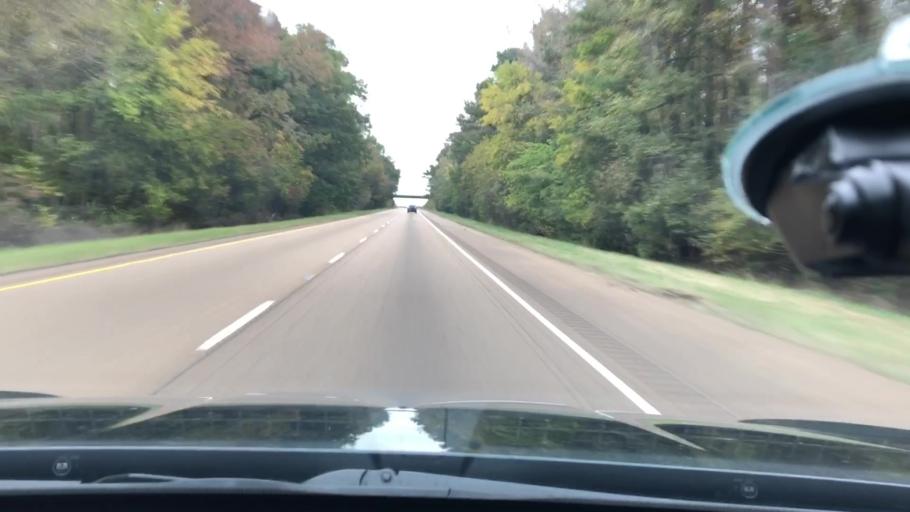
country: US
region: Arkansas
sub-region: Nevada County
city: Prescott
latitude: 33.7743
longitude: -93.4726
